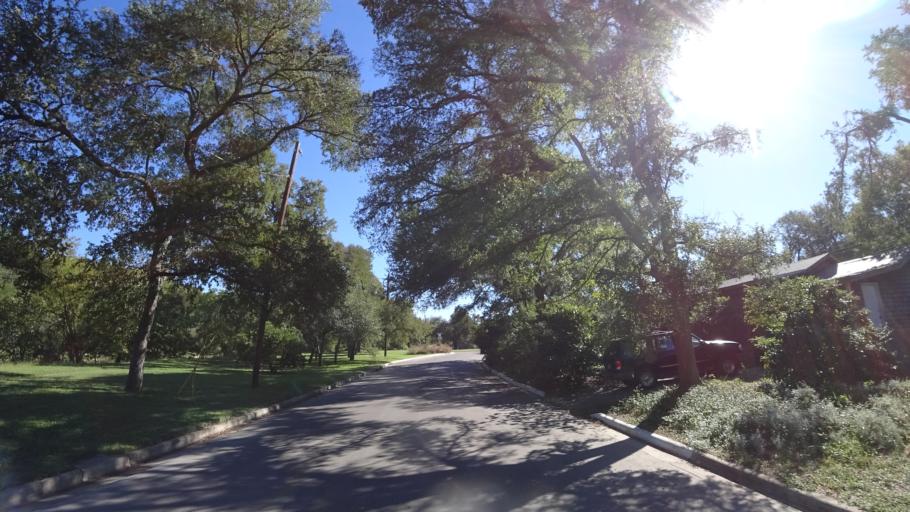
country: US
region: Texas
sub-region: Travis County
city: Austin
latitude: 30.3134
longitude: -97.7493
